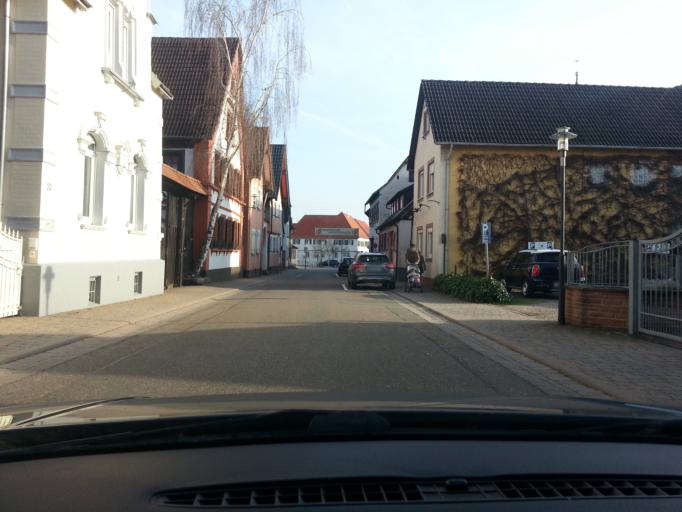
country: DE
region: Rheinland-Pfalz
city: Billigheim-Ingenheim
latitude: 49.1382
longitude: 8.0954
